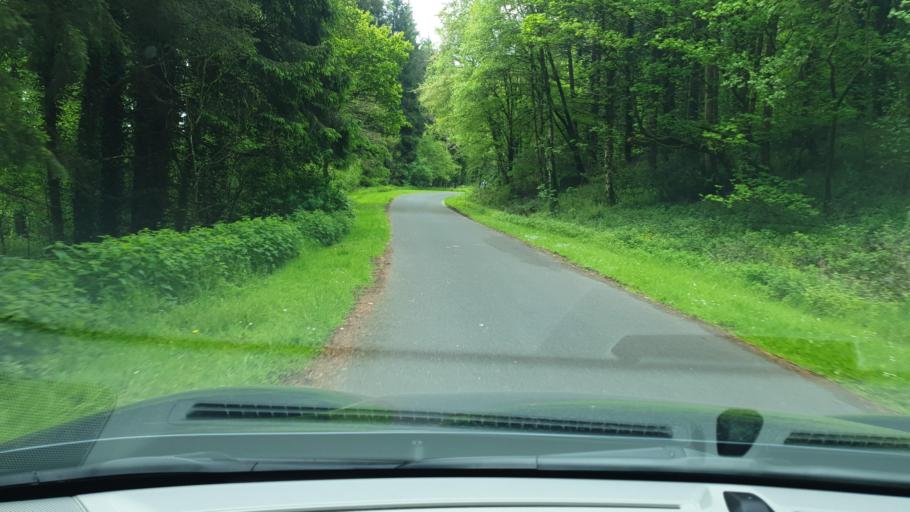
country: IE
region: Ulster
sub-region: An Cabhan
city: Kingscourt
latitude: 53.9143
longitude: -6.7887
